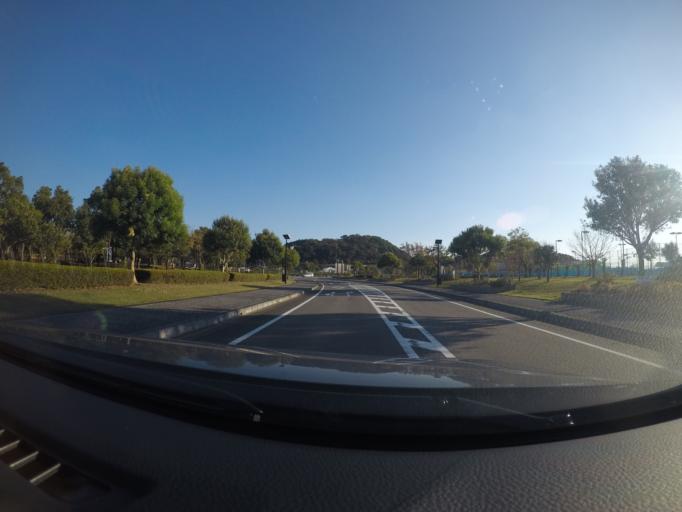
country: JP
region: Kumamoto
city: Minamata
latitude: 32.2009
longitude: 130.3818
